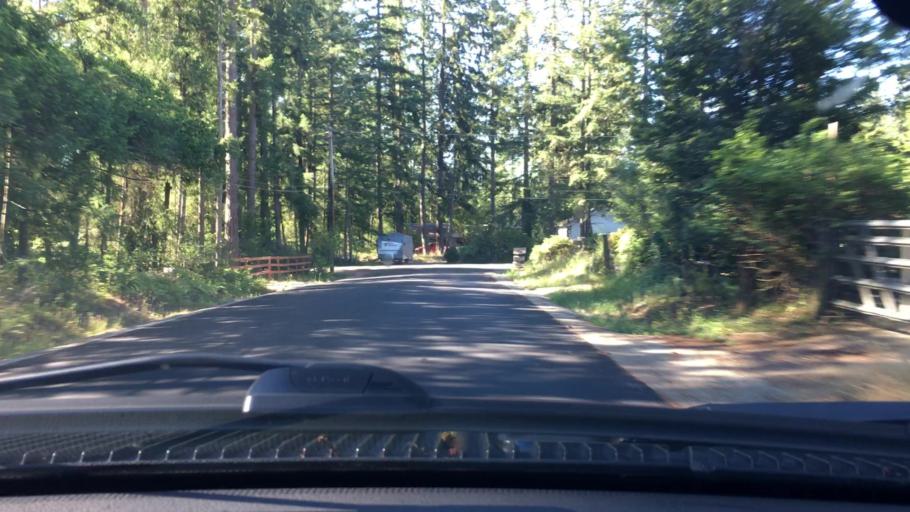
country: US
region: Washington
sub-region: King County
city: Lake Morton-Berrydale
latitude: 47.3182
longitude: -122.0993
